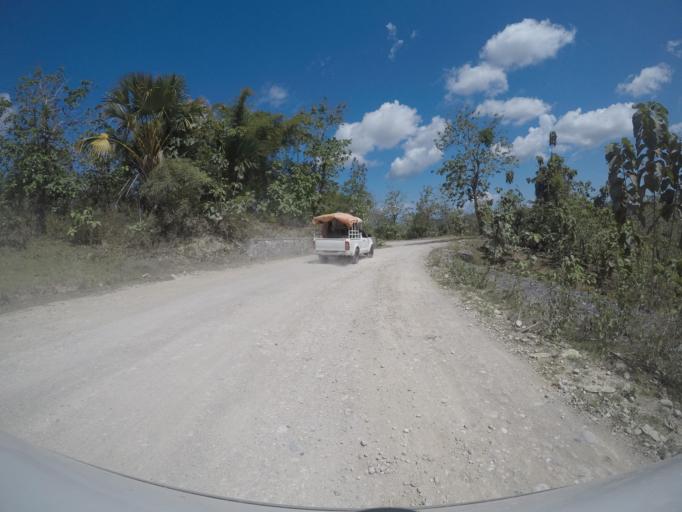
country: TL
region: Viqueque
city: Viqueque
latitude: -8.8933
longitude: 126.3863
